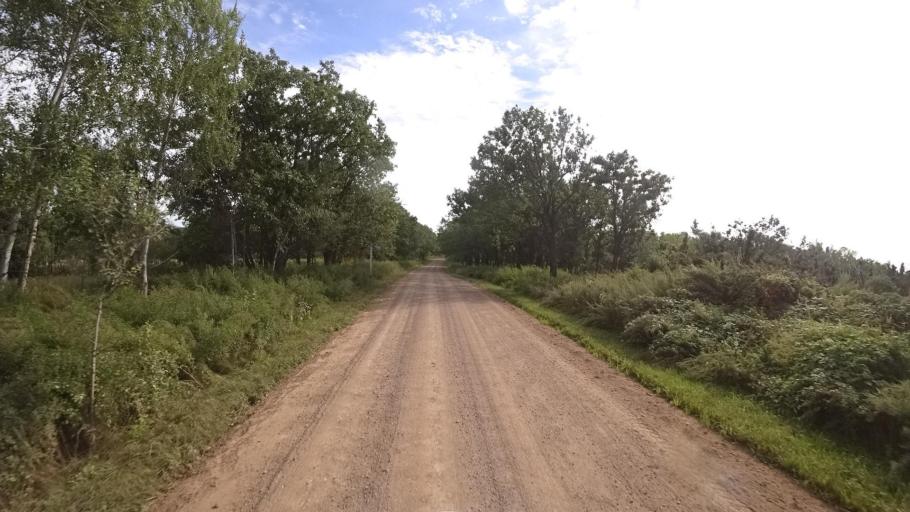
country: RU
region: Primorskiy
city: Dostoyevka
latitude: 44.3583
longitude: 133.5223
